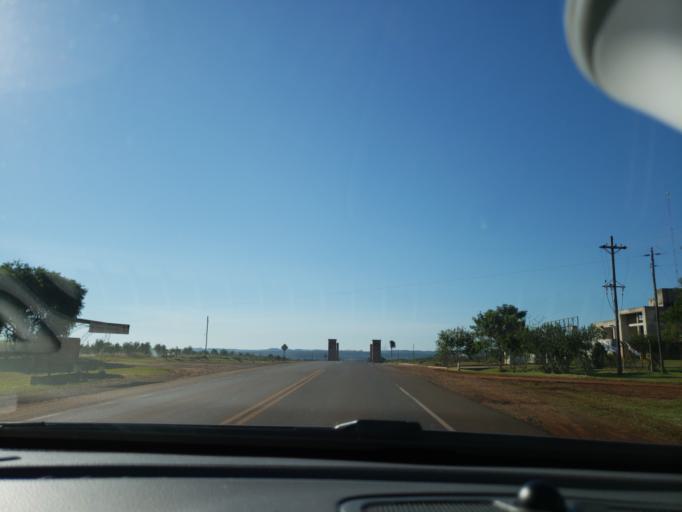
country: AR
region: Misiones
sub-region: Departamento de Apostoles
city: Apostoles
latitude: -27.8661
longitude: -55.7652
